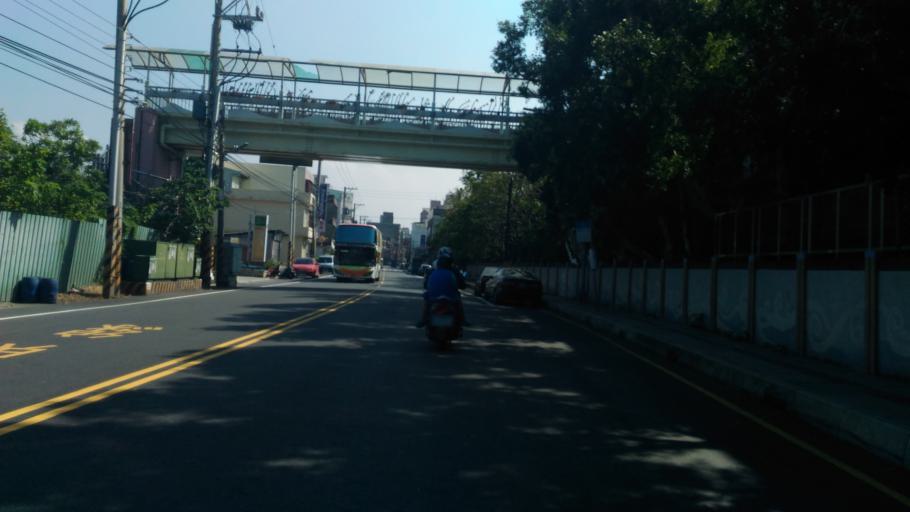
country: TW
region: Taiwan
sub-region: Hsinchu
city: Hsinchu
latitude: 24.8390
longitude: 120.9397
